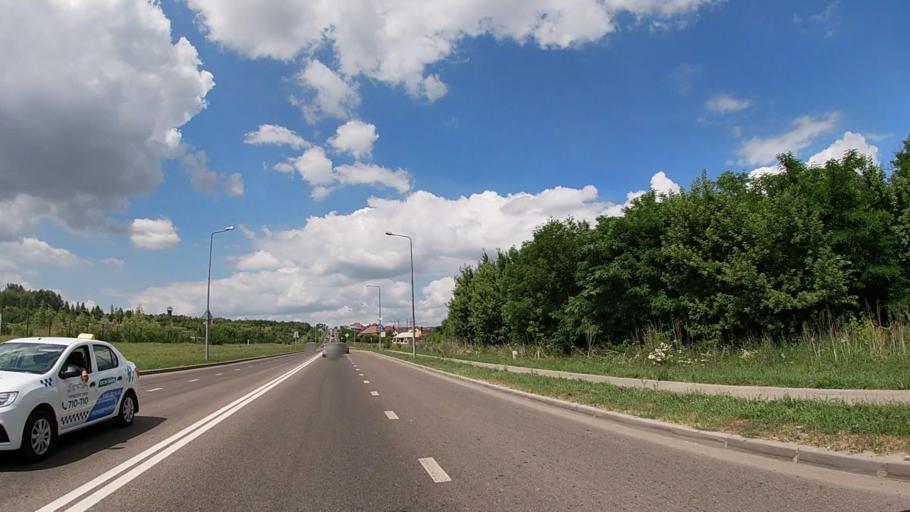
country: RU
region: Belgorod
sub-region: Belgorodskiy Rayon
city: Belgorod
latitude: 50.5951
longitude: 36.5503
